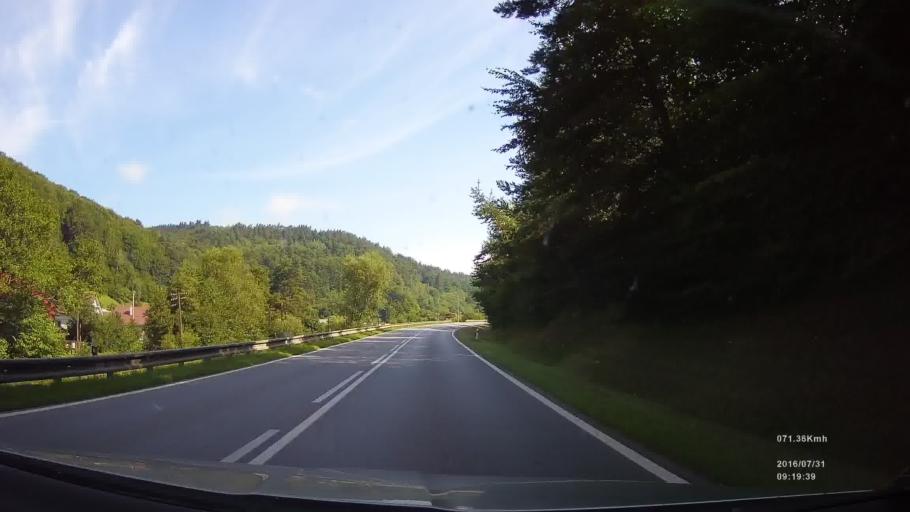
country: SK
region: Presovsky
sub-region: Okres Bardejov
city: Bardejov
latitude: 49.2668
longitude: 21.2545
